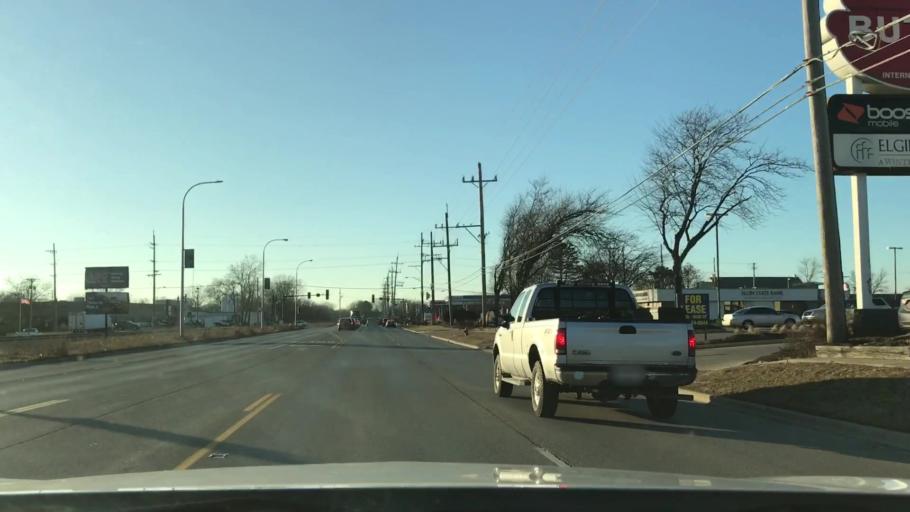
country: US
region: Illinois
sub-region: Kane County
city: Sleepy Hollow
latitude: 42.0588
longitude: -88.3136
